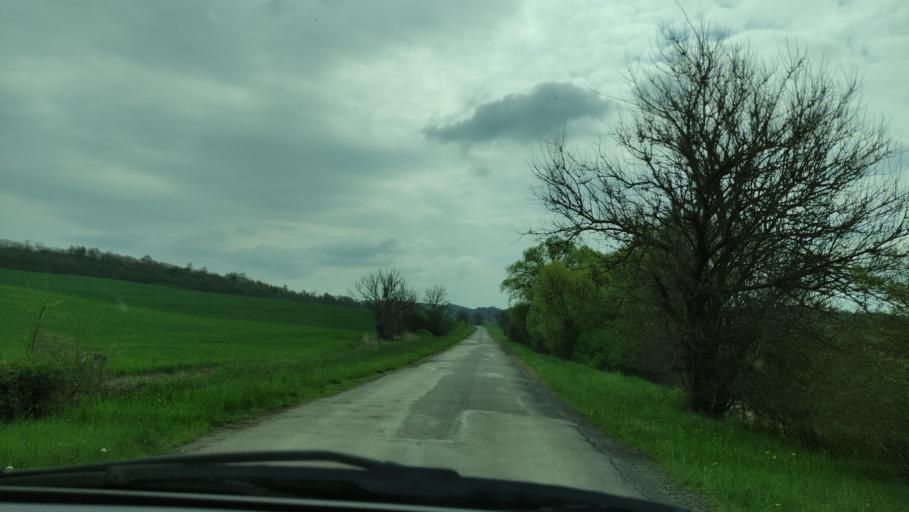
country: HU
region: Baranya
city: Magocs
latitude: 46.3059
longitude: 18.1892
